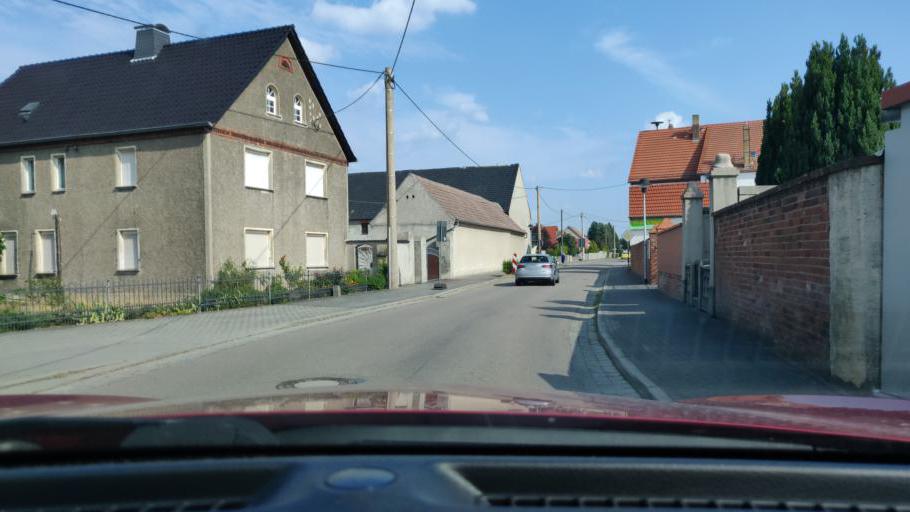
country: DE
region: Saxony
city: Mockrehna
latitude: 51.4929
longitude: 12.8311
